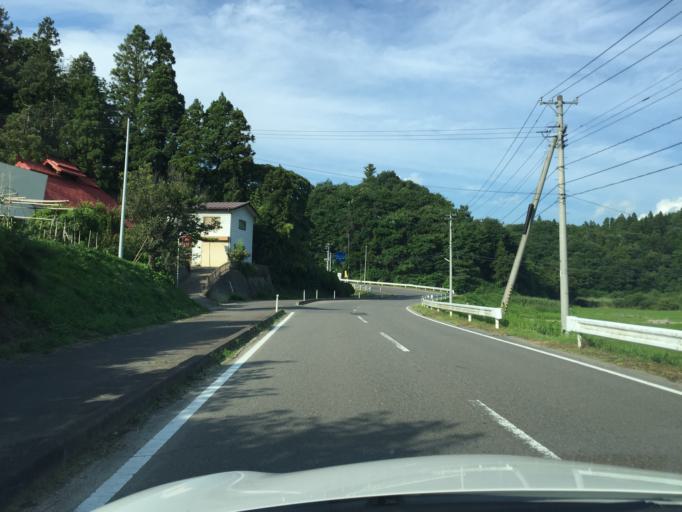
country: JP
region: Fukushima
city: Miharu
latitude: 37.3563
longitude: 140.5137
